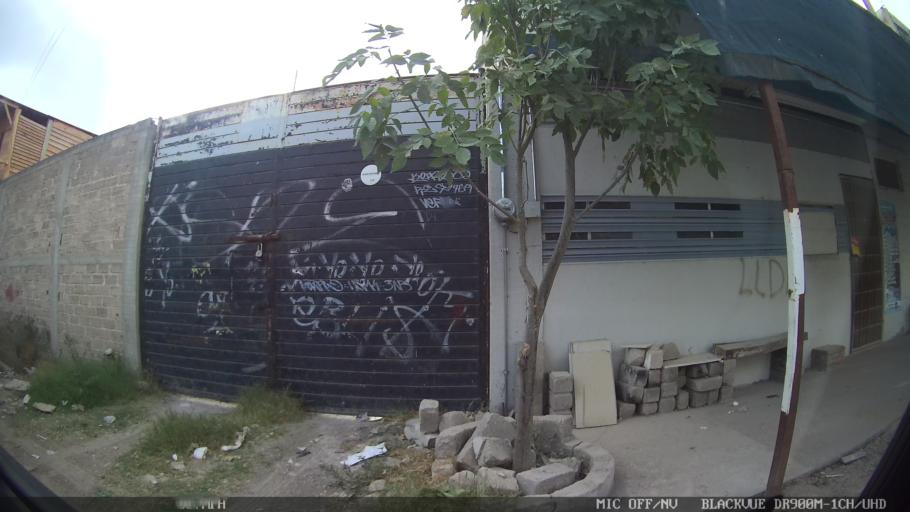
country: MX
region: Jalisco
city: Tonala
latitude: 20.6668
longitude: -103.2374
